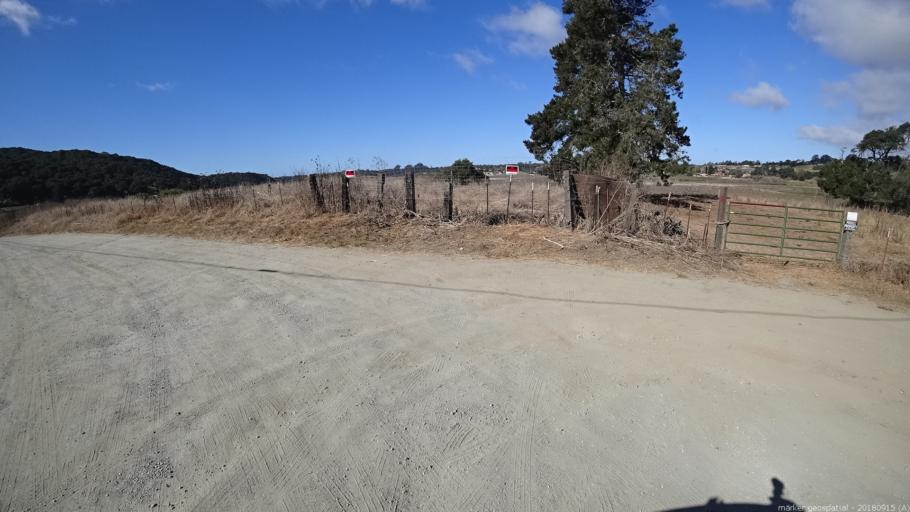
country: US
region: California
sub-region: Monterey County
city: Las Lomas
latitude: 36.8632
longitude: -121.7402
